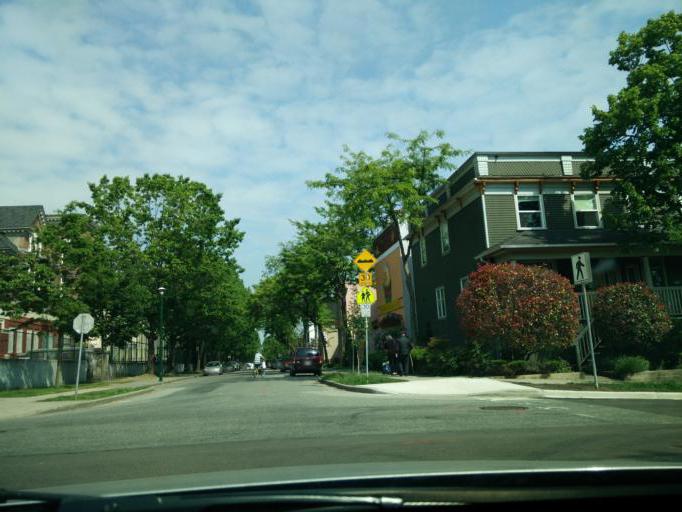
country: CA
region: British Columbia
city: Vancouver
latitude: 49.2794
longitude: -123.0937
